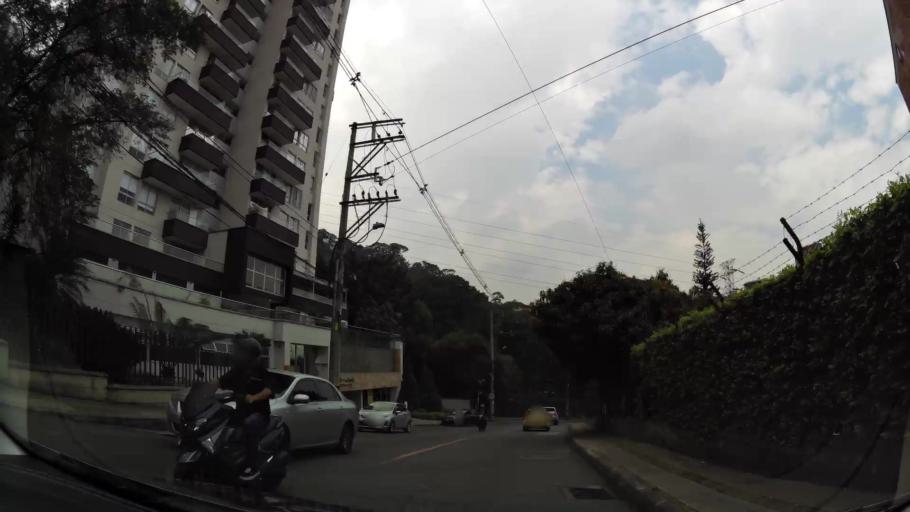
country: CO
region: Antioquia
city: Medellin
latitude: 6.2269
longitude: -75.5640
